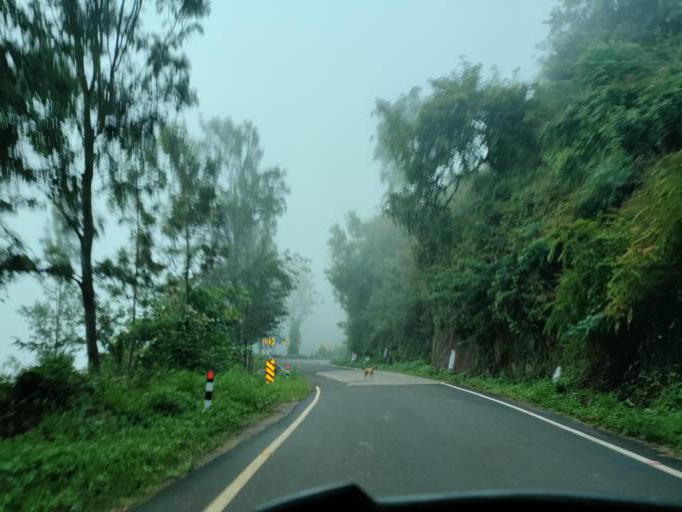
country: IN
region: Tamil Nadu
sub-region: Dindigul
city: Ayakudi
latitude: 10.3503
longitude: 77.5747
